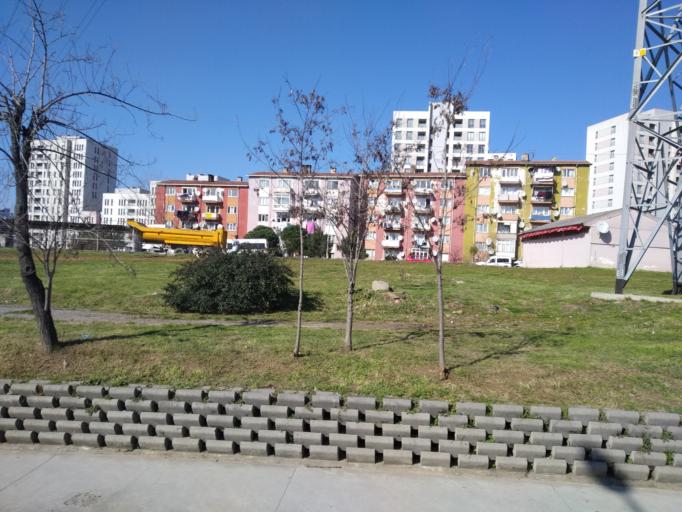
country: TR
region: Istanbul
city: Umraniye
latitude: 40.9922
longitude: 29.1523
